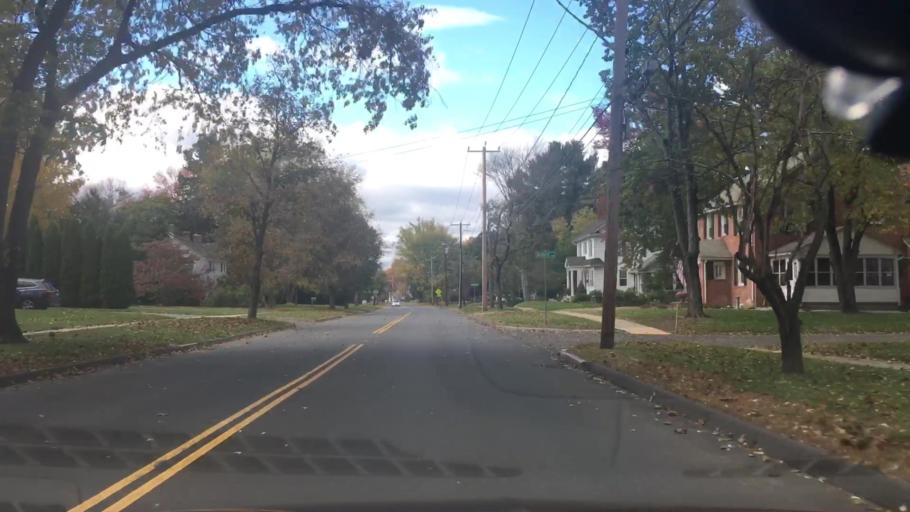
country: US
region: Connecticut
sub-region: Hartford County
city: Sherwood Manor
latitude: 42.0319
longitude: -72.5720
